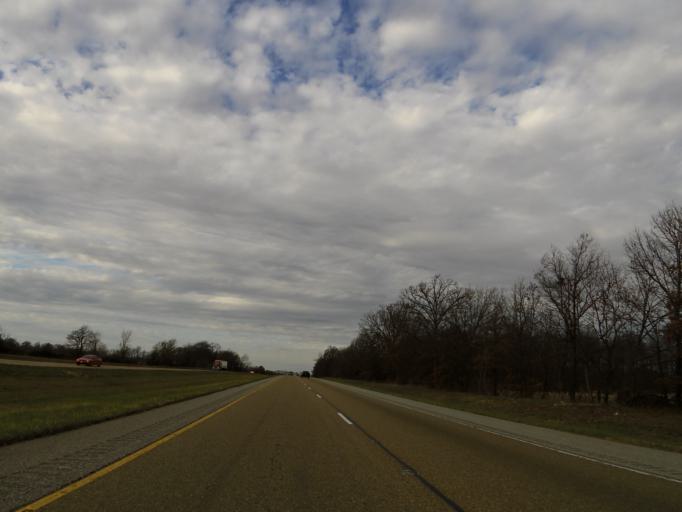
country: US
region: Illinois
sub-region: Clinton County
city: Wamac
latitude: 38.3893
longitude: -89.2084
